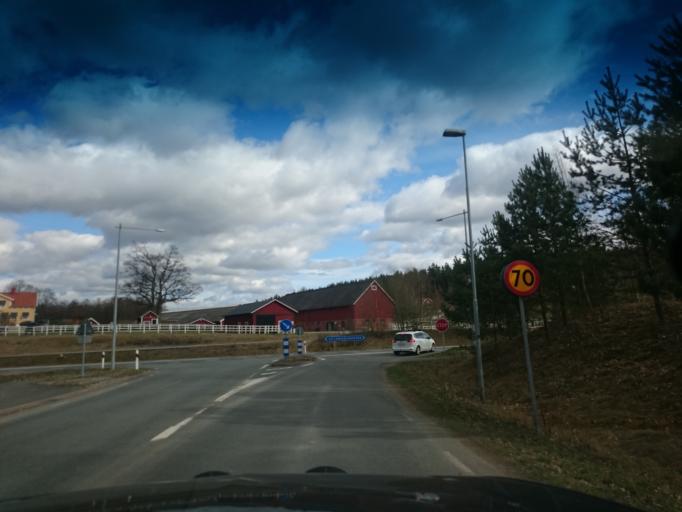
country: SE
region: Joenkoeping
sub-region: Vetlanda Kommun
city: Vetlanda
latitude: 57.3976
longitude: 15.0850
